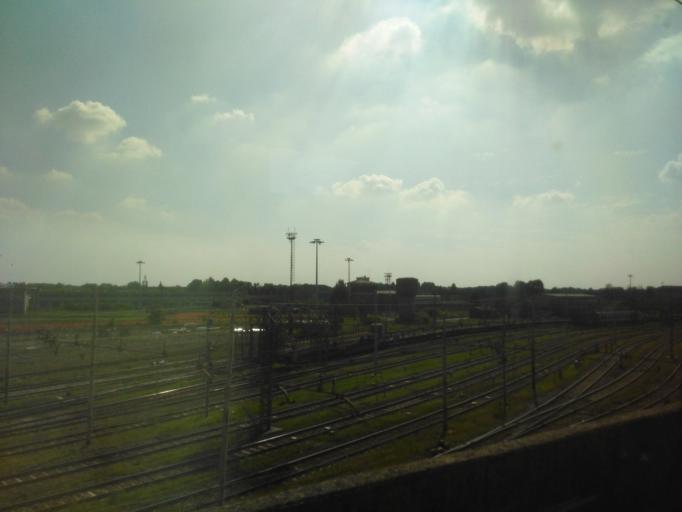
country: IT
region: Lombardy
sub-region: Citta metropolitana di Milano
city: Novegro-Tregarezzo-San Felice
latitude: 45.4769
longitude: 9.2787
